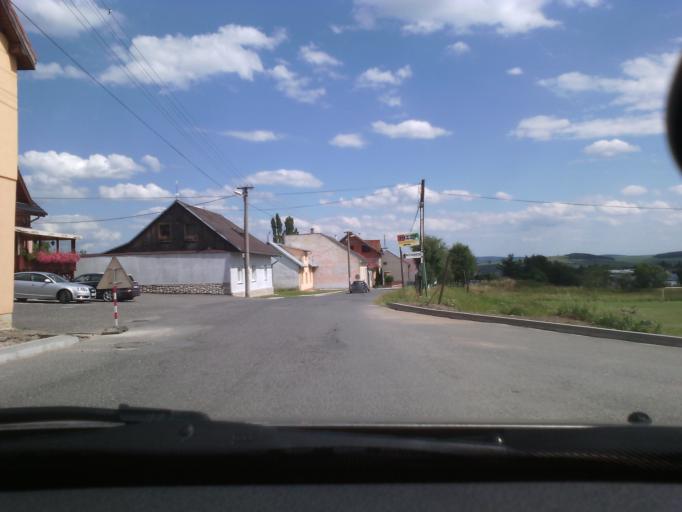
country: SK
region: Presovsky
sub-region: Okres Poprad
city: Nova Lesna
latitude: 49.1354
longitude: 20.3096
